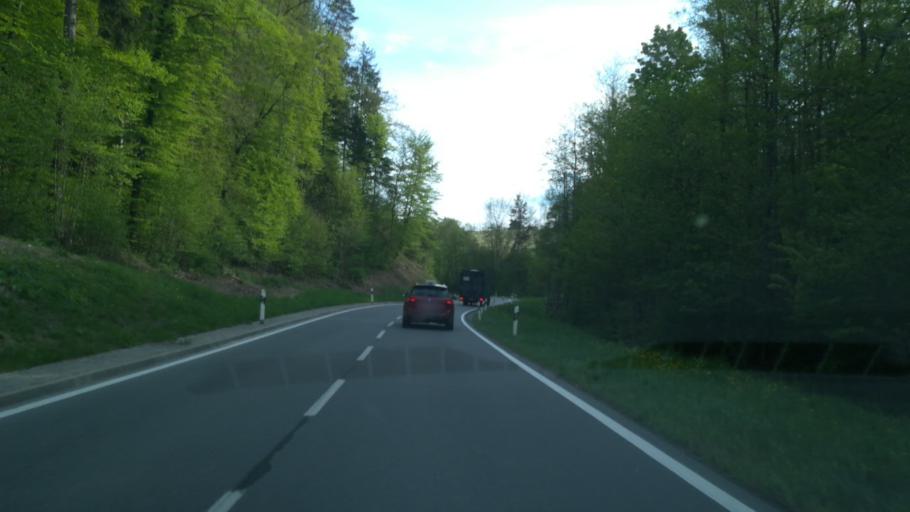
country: DE
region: Baden-Wuerttemberg
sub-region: Freiburg Region
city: Muhlingen
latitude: 47.8995
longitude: 9.0078
